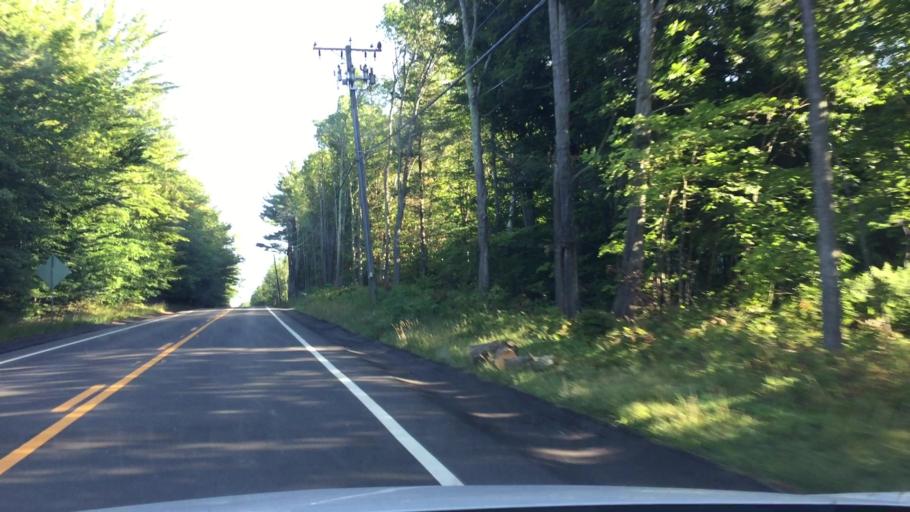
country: US
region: Massachusetts
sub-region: Berkshire County
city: Becket
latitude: 42.2680
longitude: -73.0521
